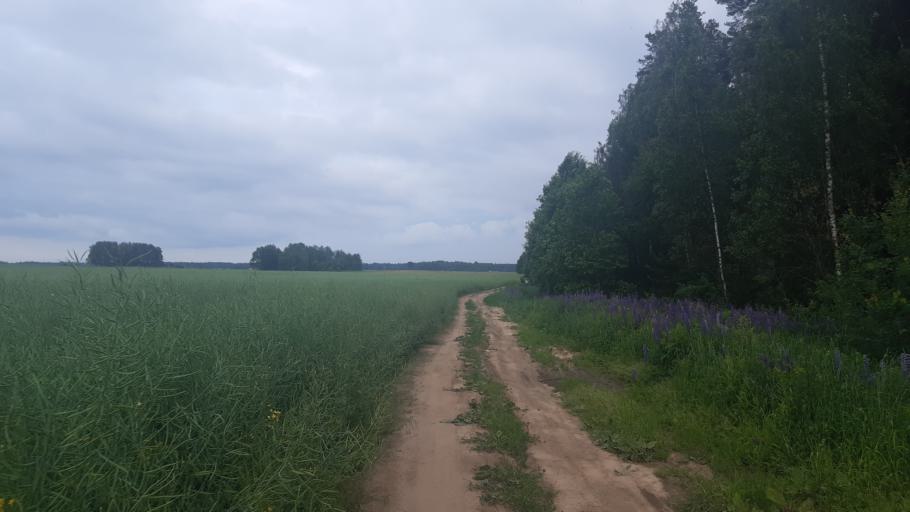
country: BY
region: Minsk
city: Horad Zhodzina
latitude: 54.1361
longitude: 28.2830
